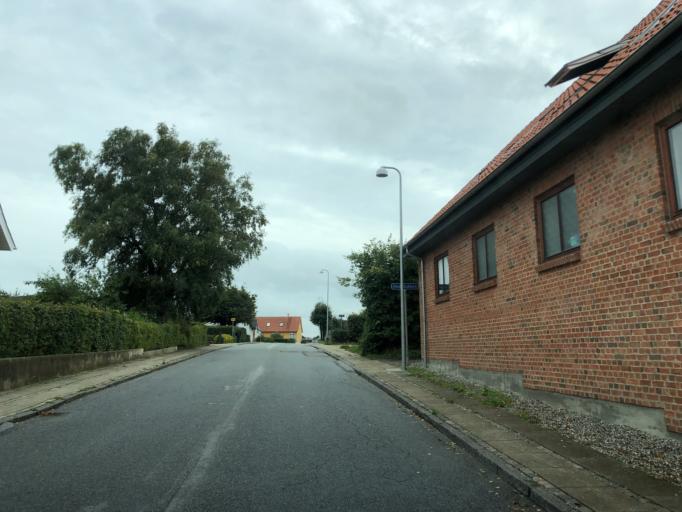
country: DK
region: Central Jutland
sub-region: Herning Kommune
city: Vildbjerg
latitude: 56.1780
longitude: 8.7436
